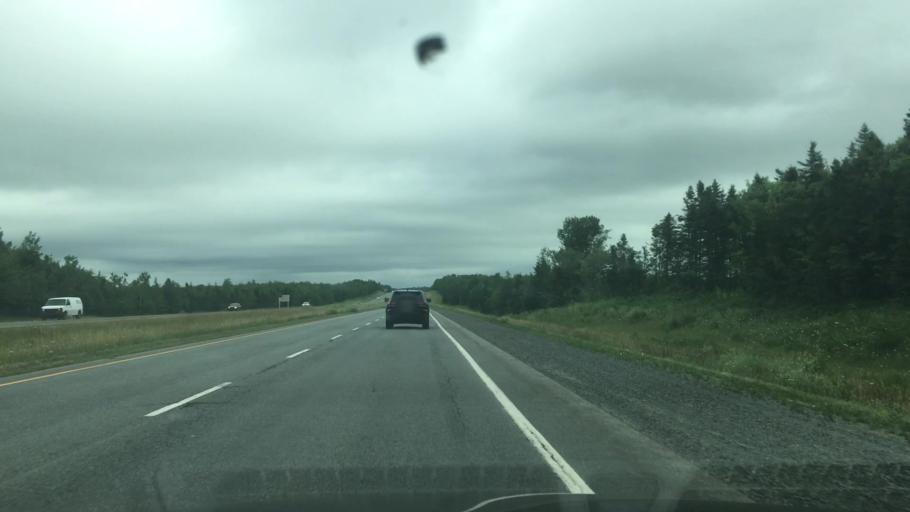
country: CA
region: Nova Scotia
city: Cole Harbour
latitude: 44.9947
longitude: -63.4927
